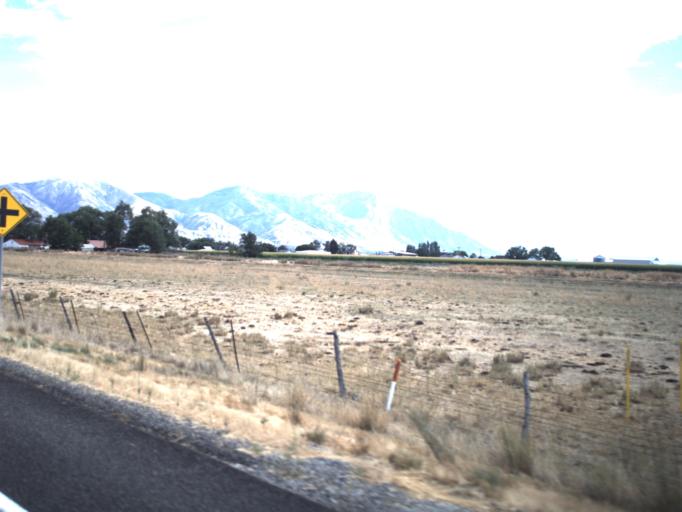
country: US
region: Utah
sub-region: Box Elder County
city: Honeyville
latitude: 41.5556
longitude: -112.1319
